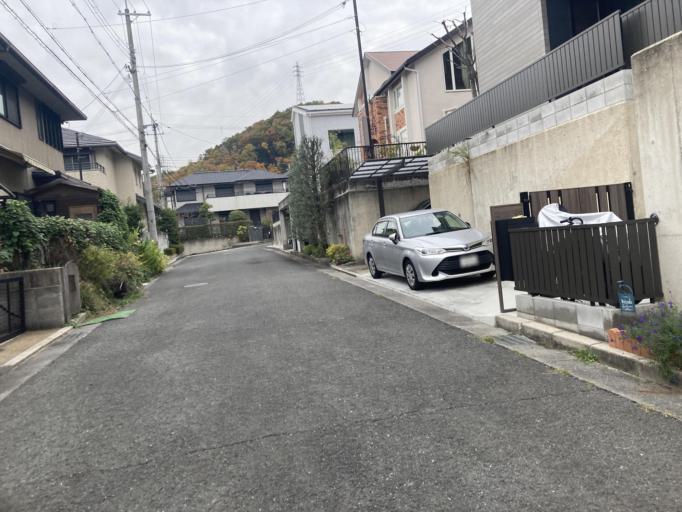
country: JP
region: Nara
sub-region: Ikoma-shi
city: Ikoma
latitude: 34.6745
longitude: 135.7203
